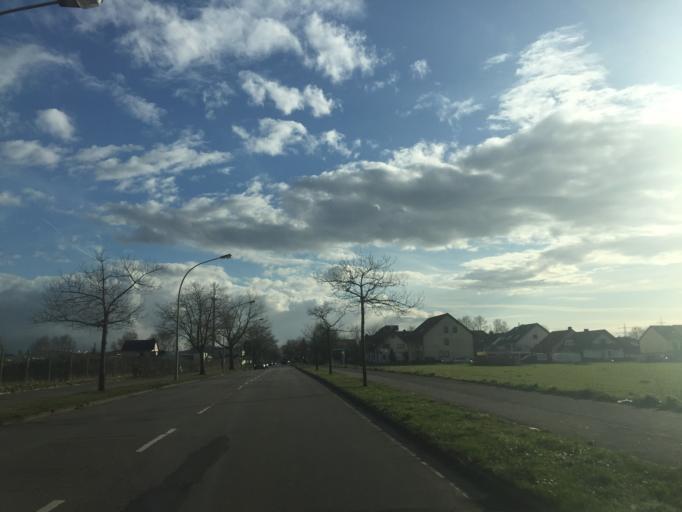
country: DE
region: Baden-Wuerttemberg
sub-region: Karlsruhe Region
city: Ladenburg
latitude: 49.4807
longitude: 8.5998
